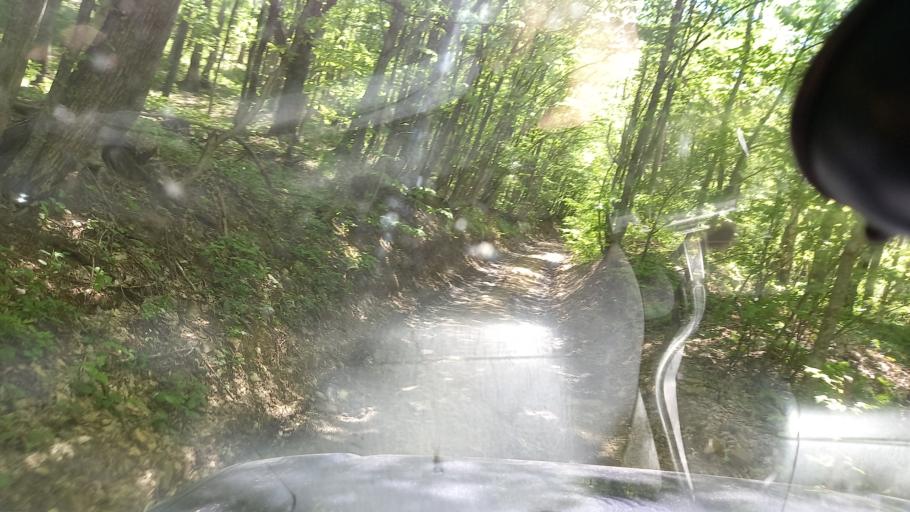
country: RU
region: Krasnodarskiy
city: Tuapse
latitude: 44.2563
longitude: 39.2840
